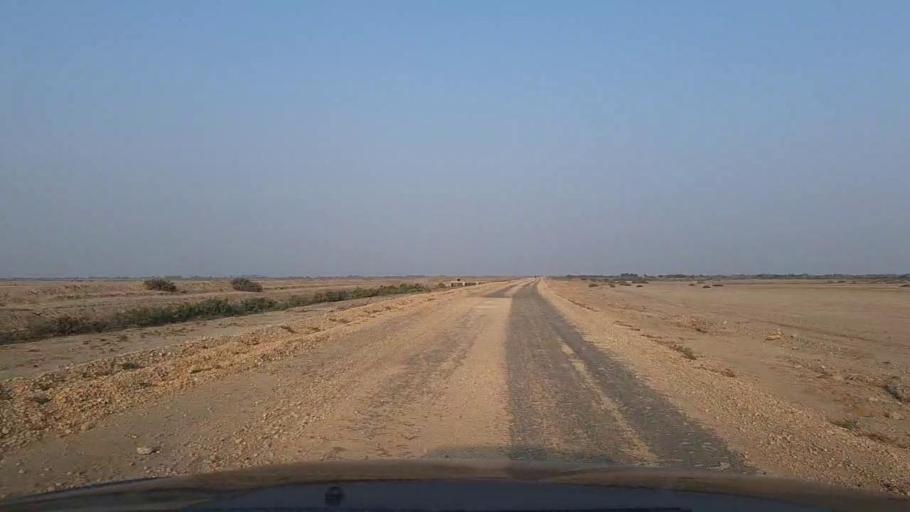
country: PK
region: Sindh
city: Mirpur Sakro
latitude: 24.4331
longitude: 67.7626
